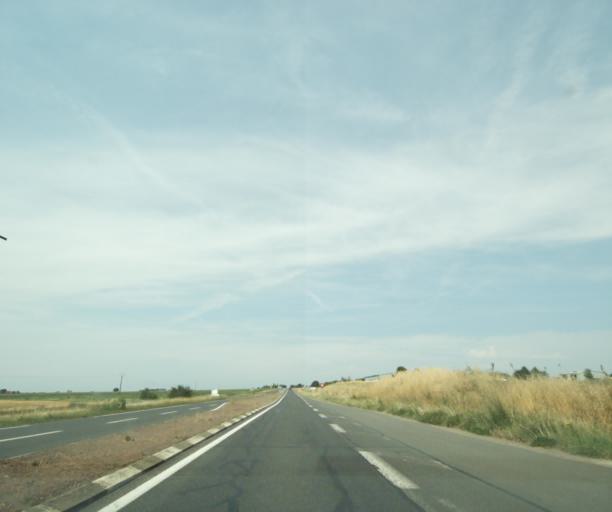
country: FR
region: Centre
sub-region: Departement d'Indre-et-Loire
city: Sainte-Maure-de-Touraine
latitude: 47.1599
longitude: 0.6476
